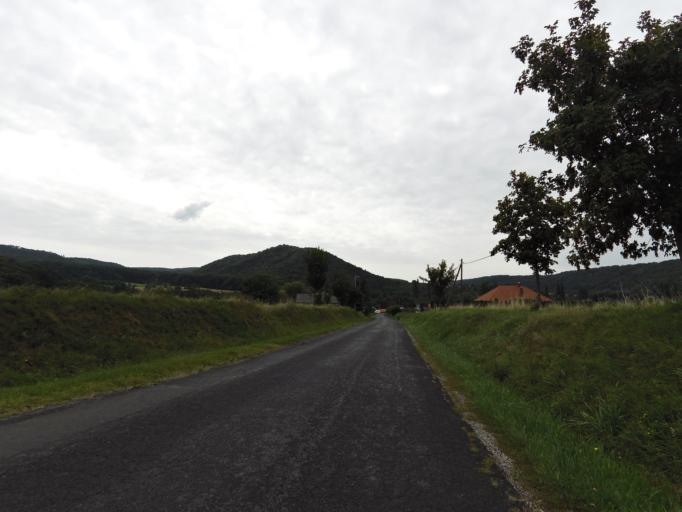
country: HU
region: Zala
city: Gyenesdias
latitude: 46.8491
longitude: 17.3033
